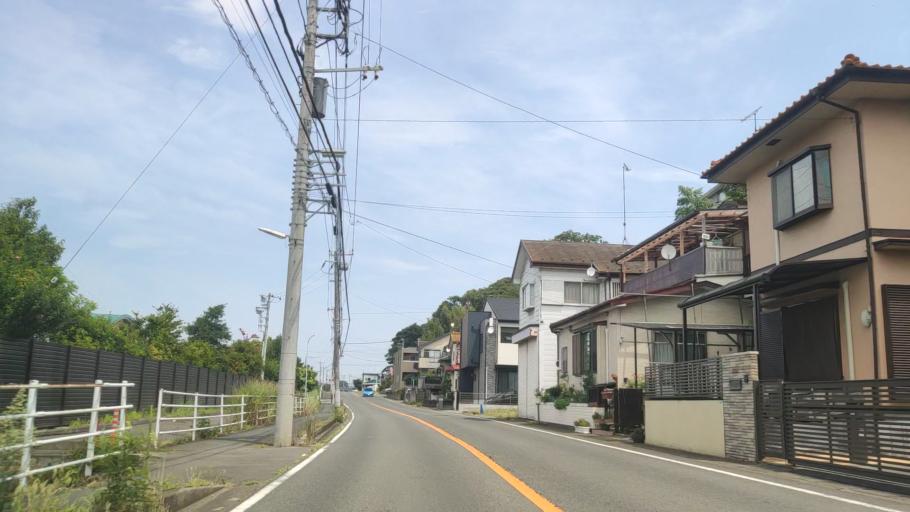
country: JP
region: Kanagawa
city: Atsugi
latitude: 35.4339
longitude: 139.3925
